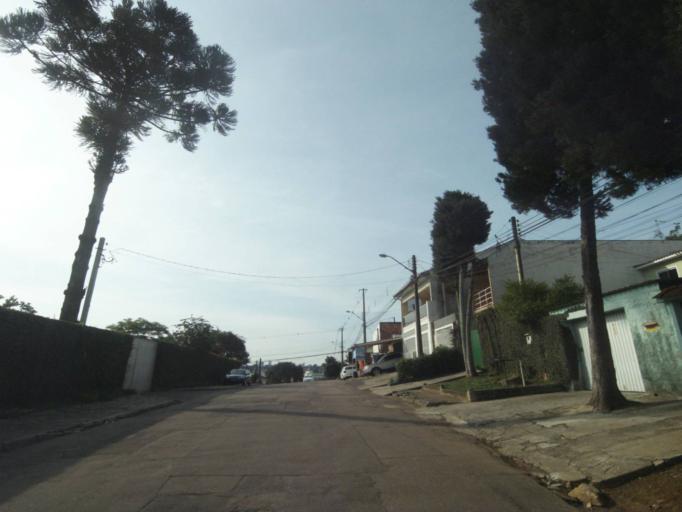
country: BR
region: Parana
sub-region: Curitiba
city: Curitiba
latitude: -25.4639
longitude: -49.3140
